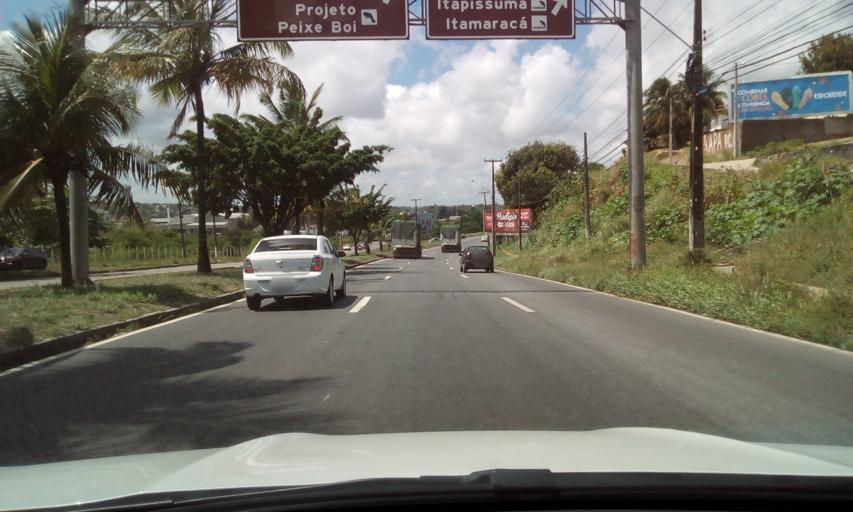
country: BR
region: Pernambuco
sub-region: Igarassu
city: Igarassu
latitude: -7.8377
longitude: -34.9123
